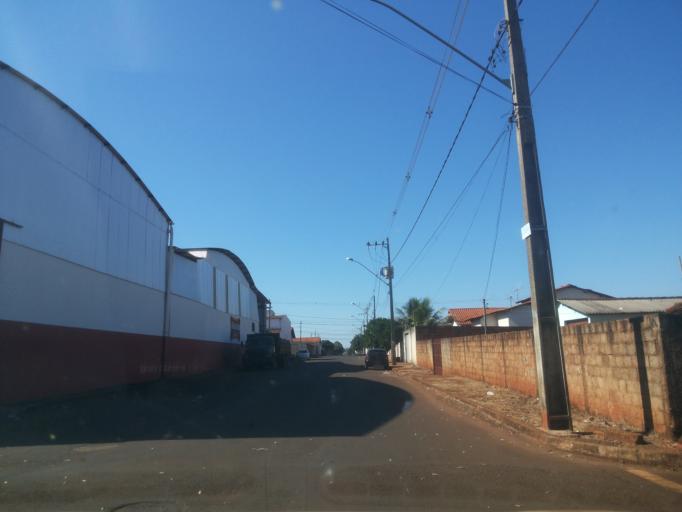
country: BR
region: Minas Gerais
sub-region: Centralina
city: Centralina
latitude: -18.7286
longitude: -49.2007
